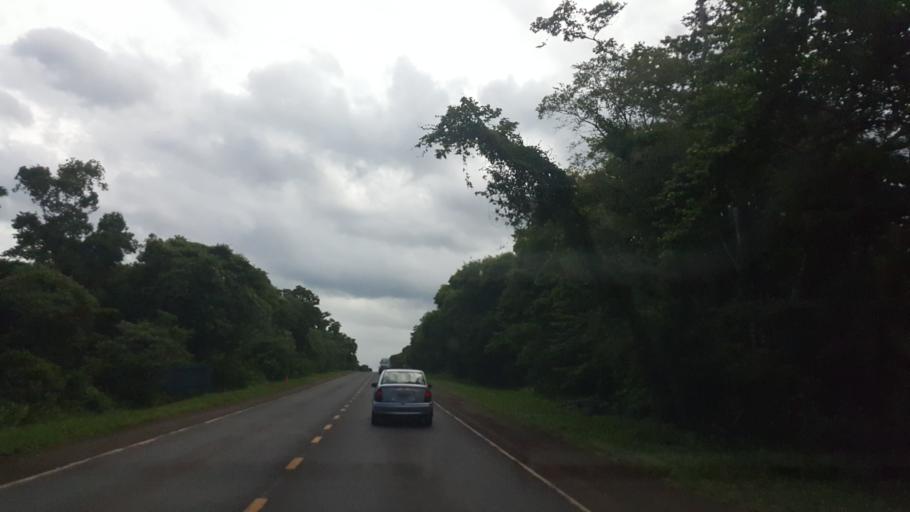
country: AR
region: Misiones
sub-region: Departamento de Iguazu
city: Puerto Iguazu
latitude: -25.7254
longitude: -54.5277
